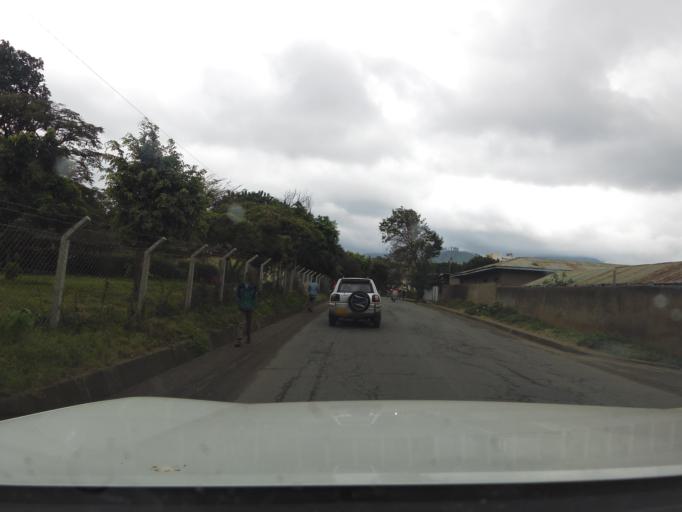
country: TZ
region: Arusha
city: Arusha
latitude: -3.3635
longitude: 36.6891
